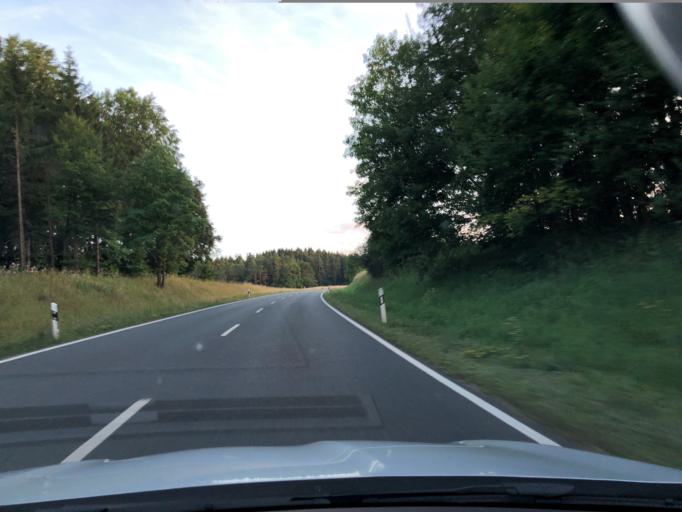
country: DE
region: Bavaria
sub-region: Upper Palatinate
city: Illschwang
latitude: 49.4348
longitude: 11.6586
